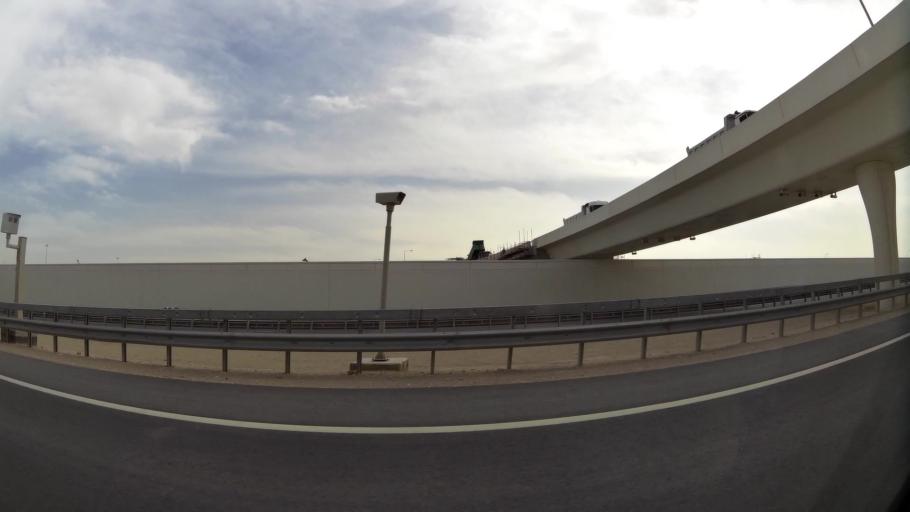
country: QA
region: Baladiyat ar Rayyan
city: Ar Rayyan
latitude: 25.3216
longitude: 51.3511
